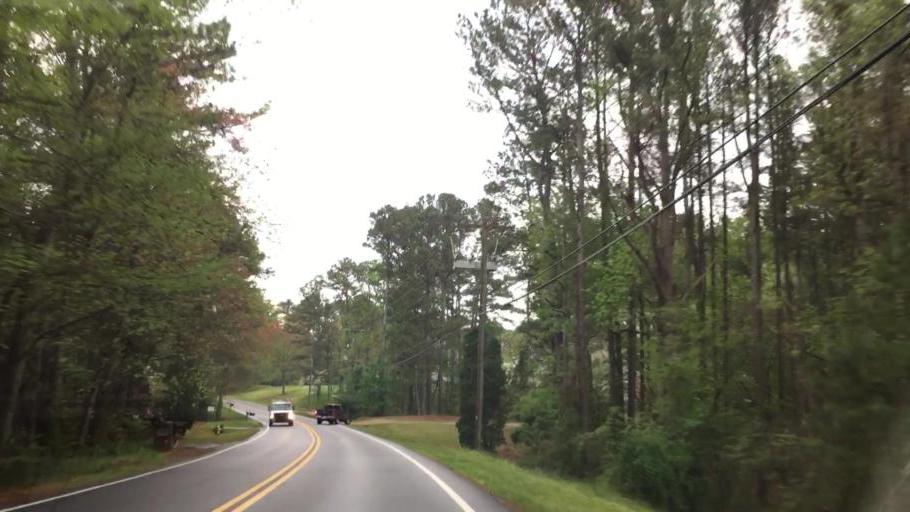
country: US
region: Georgia
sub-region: Fulton County
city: Milton
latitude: 34.1711
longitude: -84.2939
